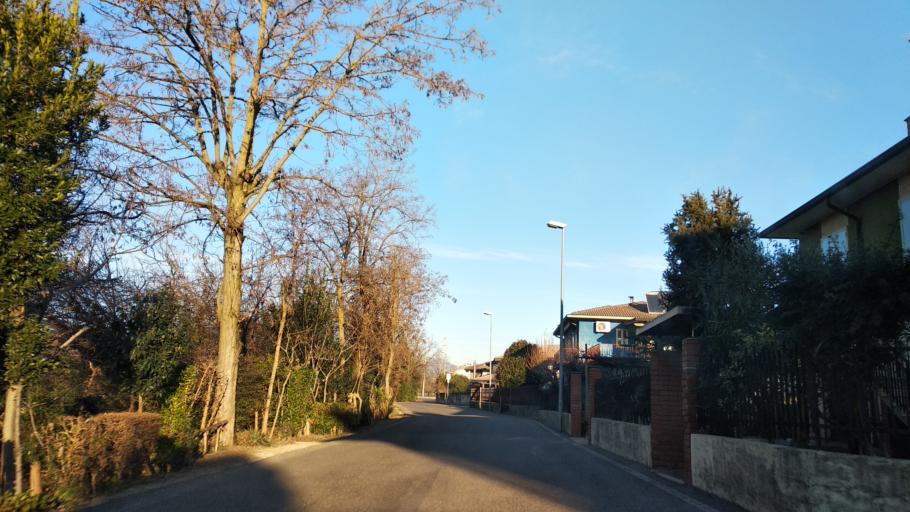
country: IT
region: Veneto
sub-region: Provincia di Vicenza
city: Crispi Cavour
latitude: 45.5900
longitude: 11.5258
